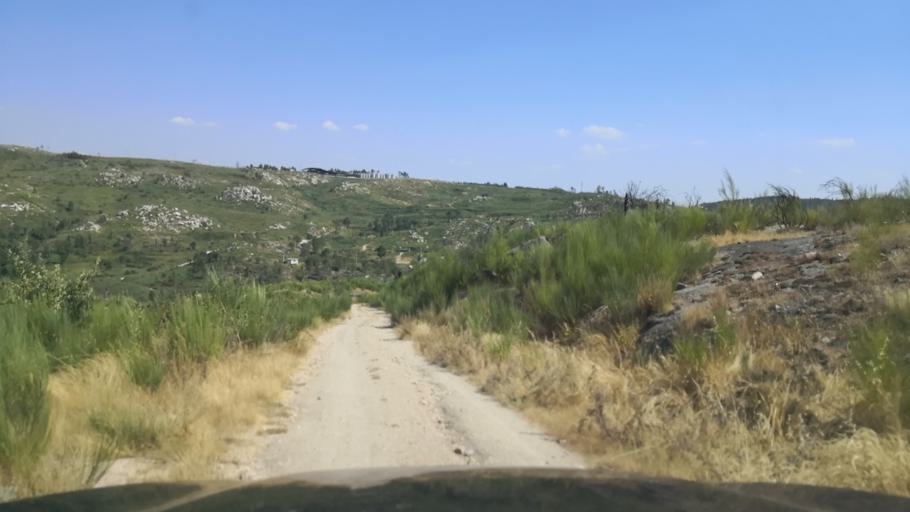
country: PT
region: Vila Real
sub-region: Sabrosa
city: Sabrosa
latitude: 41.3144
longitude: -7.4923
